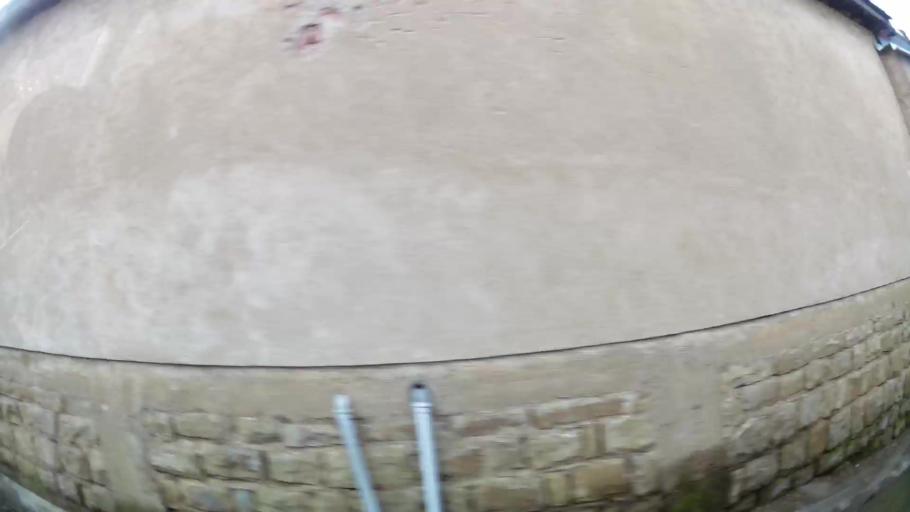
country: XK
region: Pristina
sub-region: Komuna e Prishtines
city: Pristina
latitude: 42.6770
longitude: 21.1565
